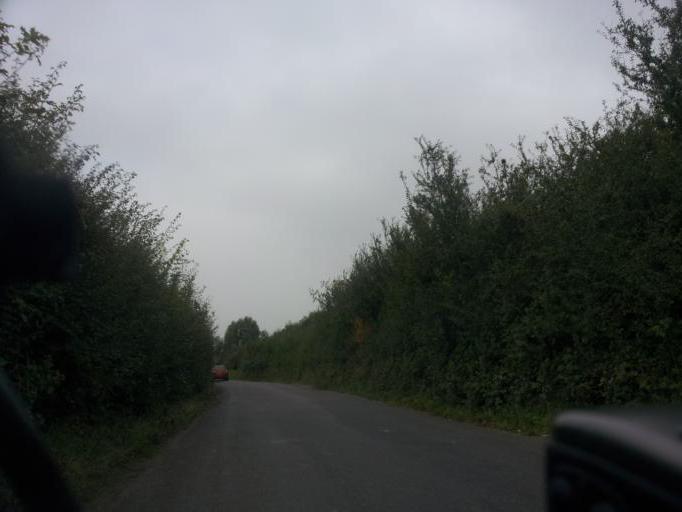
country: GB
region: England
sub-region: Kent
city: Sittingbourne
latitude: 51.3605
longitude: 0.7150
